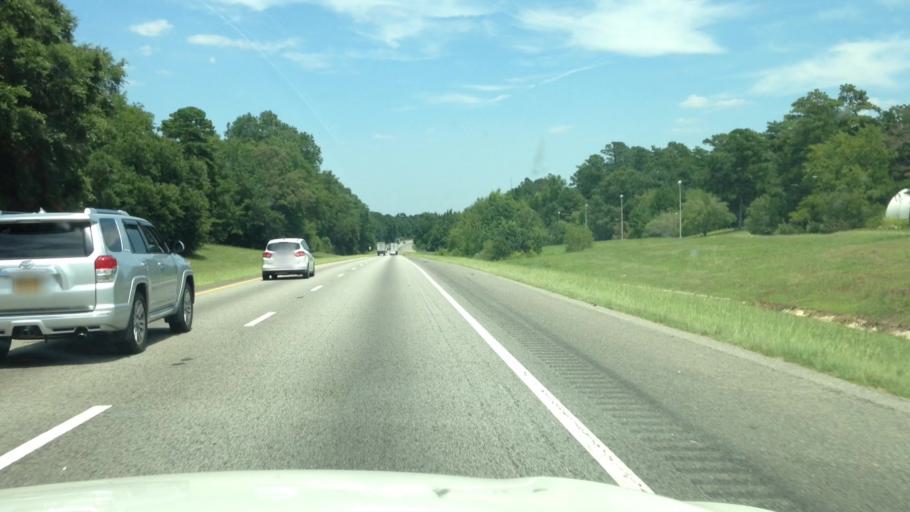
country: US
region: South Carolina
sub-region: Florence County
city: Florence
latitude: 34.2782
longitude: -79.6871
